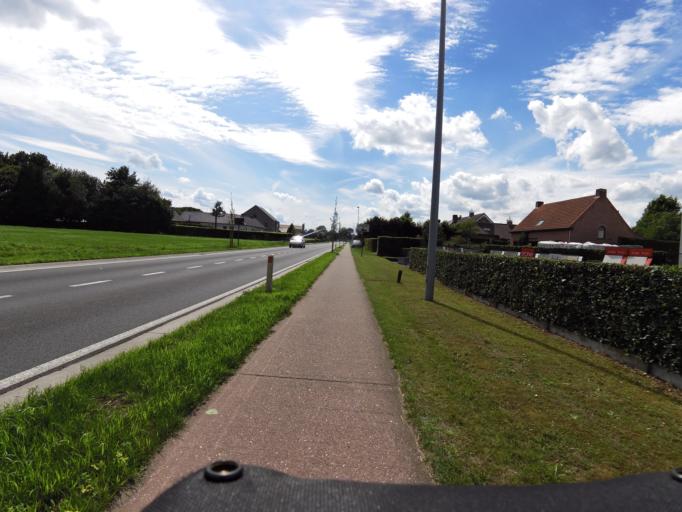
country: BE
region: Flanders
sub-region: Provincie Antwerpen
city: Hoogstraten
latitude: 51.4291
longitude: 4.7635
